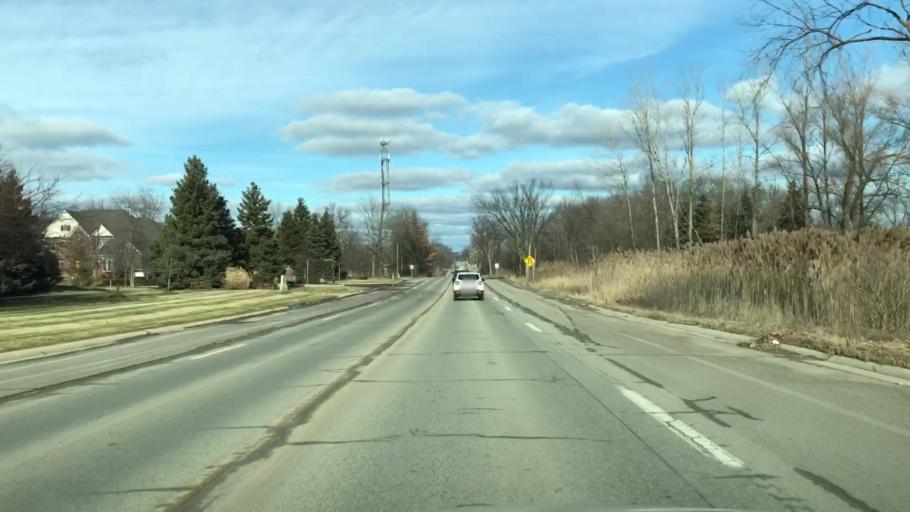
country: US
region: Michigan
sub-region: Oakland County
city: Auburn Hills
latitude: 42.7302
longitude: -83.1965
